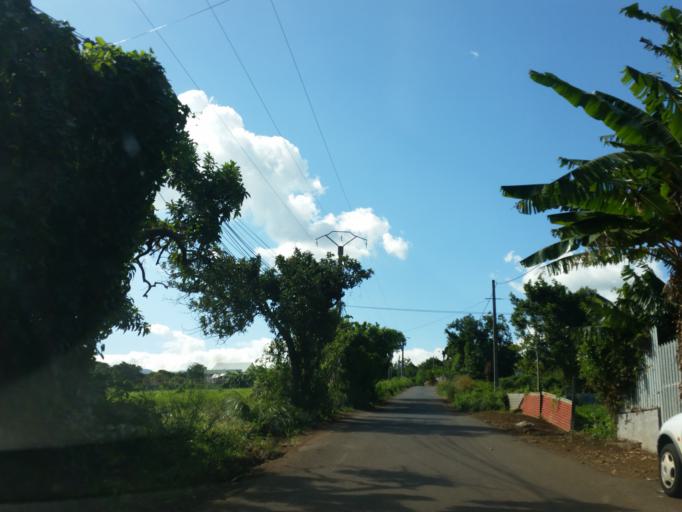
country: RE
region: Reunion
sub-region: Reunion
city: Saint-Pierre
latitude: -21.3229
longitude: 55.5008
